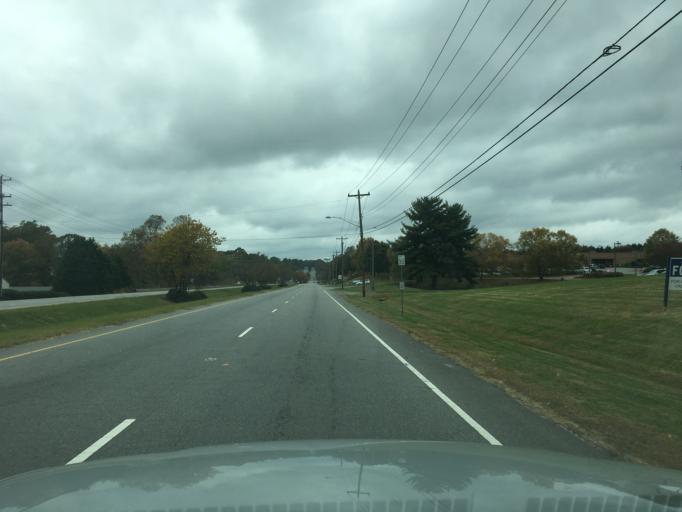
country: US
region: North Carolina
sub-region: Catawba County
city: Hickory
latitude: 35.7283
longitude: -81.3024
